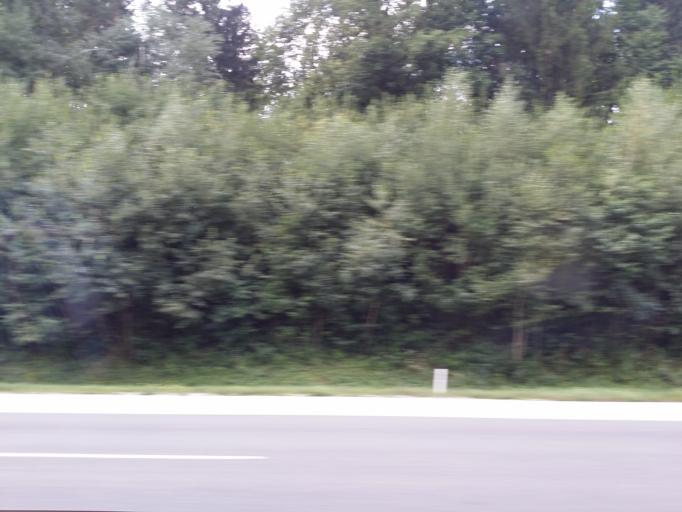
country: SI
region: Kranj
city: Kokrica
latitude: 46.2610
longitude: 14.3622
